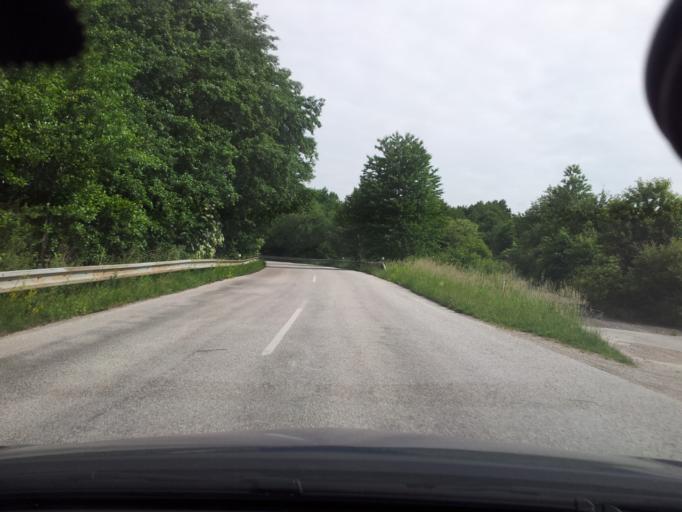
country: SK
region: Nitriansky
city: Zlate Moravce
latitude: 48.5068
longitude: 18.4331
